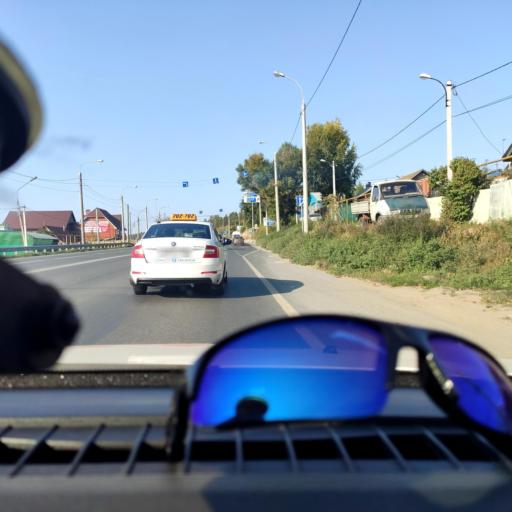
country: RU
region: Samara
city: Volzhskiy
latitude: 53.4299
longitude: 50.1190
